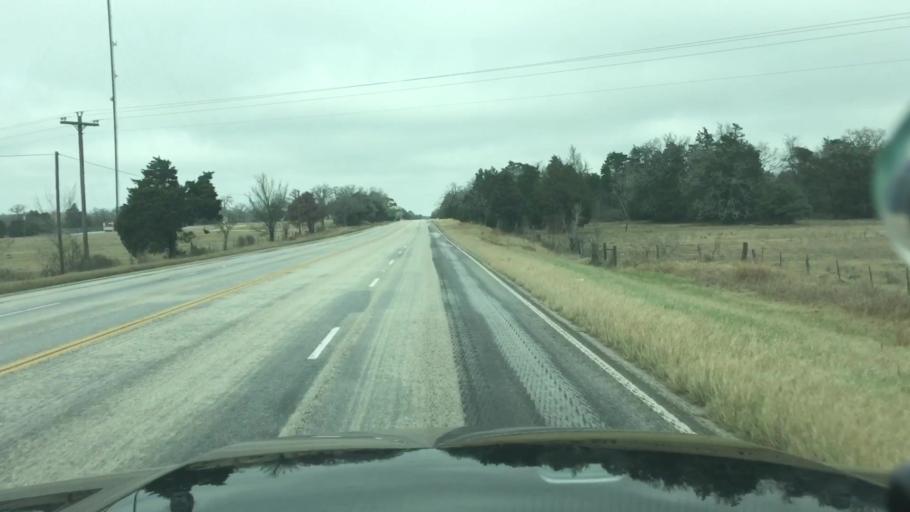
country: US
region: Texas
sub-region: Lee County
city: Giddings
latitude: 30.1066
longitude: -96.9145
